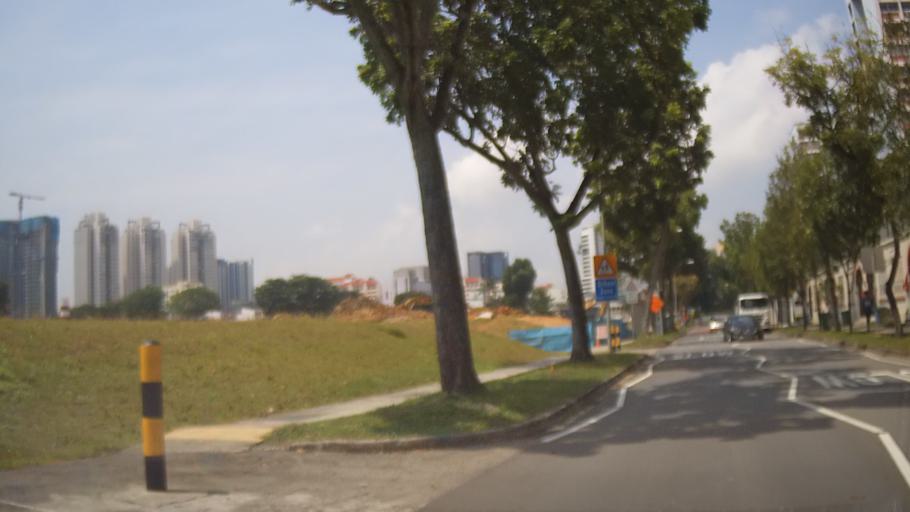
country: SG
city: Singapore
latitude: 1.3194
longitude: 103.8580
